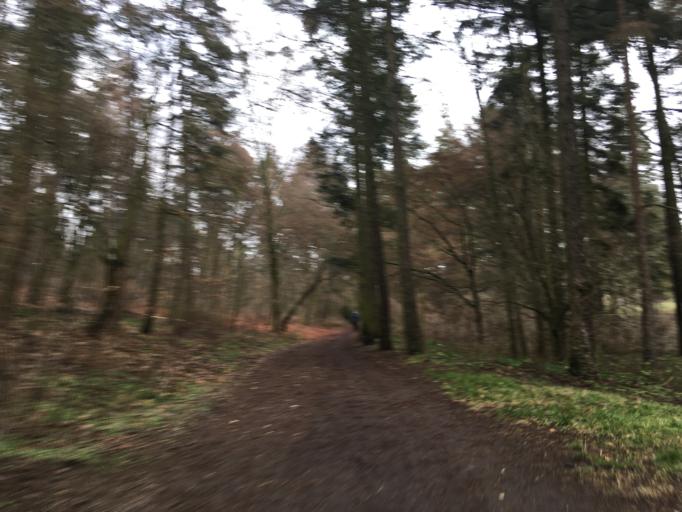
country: DE
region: Berlin
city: Reinickendorf
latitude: 52.5495
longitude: 13.3349
